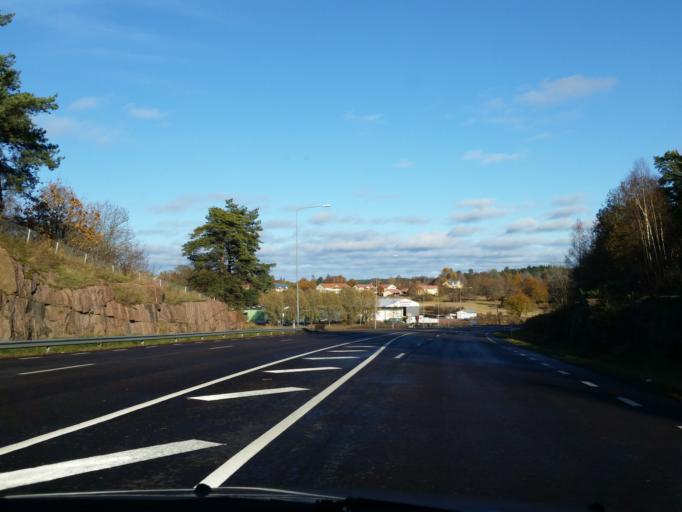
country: AX
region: Alands landsbygd
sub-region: Finstroem
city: Finstroem
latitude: 60.2270
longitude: 19.9873
